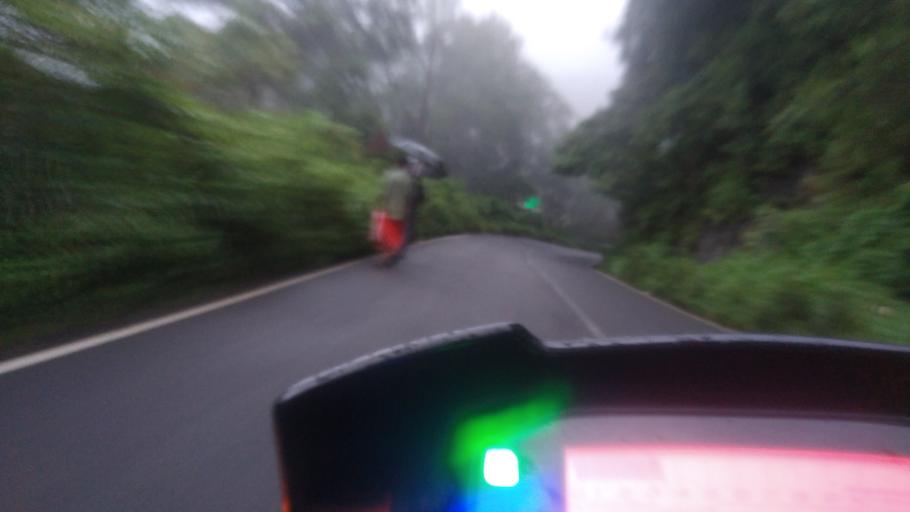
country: IN
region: Kerala
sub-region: Kottayam
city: Erattupetta
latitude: 9.5541
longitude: 76.9739
